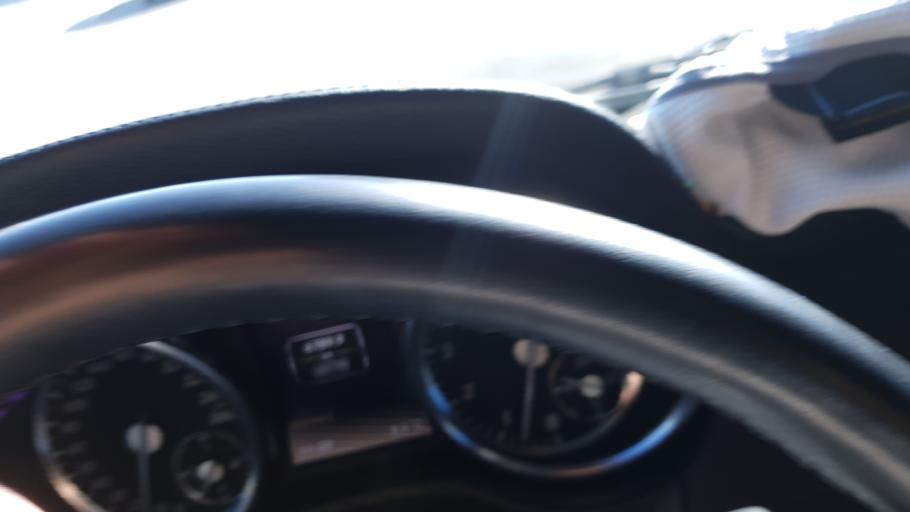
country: MN
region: Ulaanbaatar
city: Ulaanbaatar
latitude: 47.9239
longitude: 106.9488
